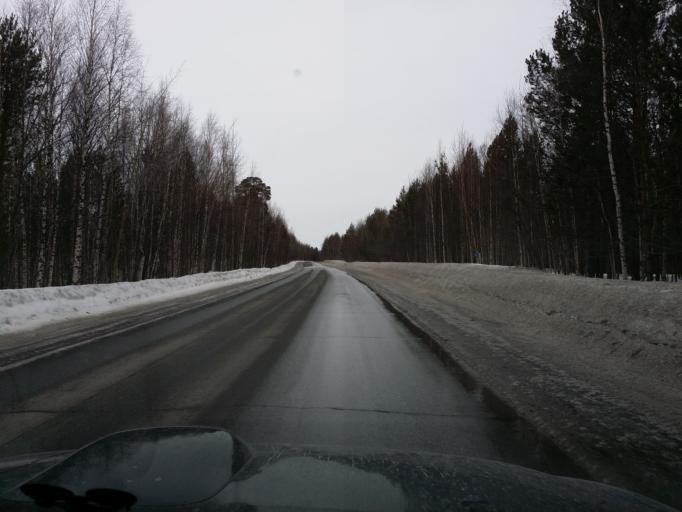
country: RU
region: Tomsk
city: Strezhevoy
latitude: 60.7955
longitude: 77.3108
